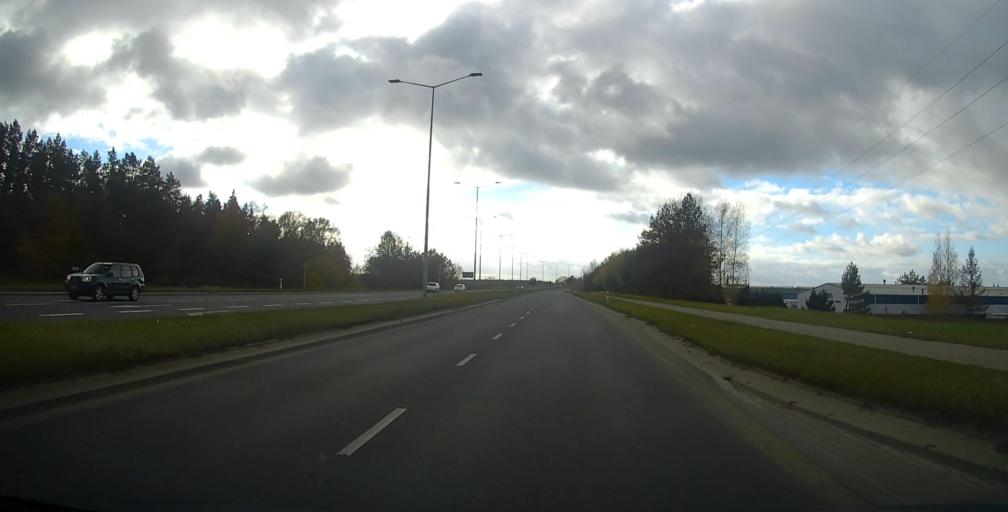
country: PL
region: Warmian-Masurian Voivodeship
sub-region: Powiat elcki
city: Elk
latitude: 53.8112
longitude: 22.3782
